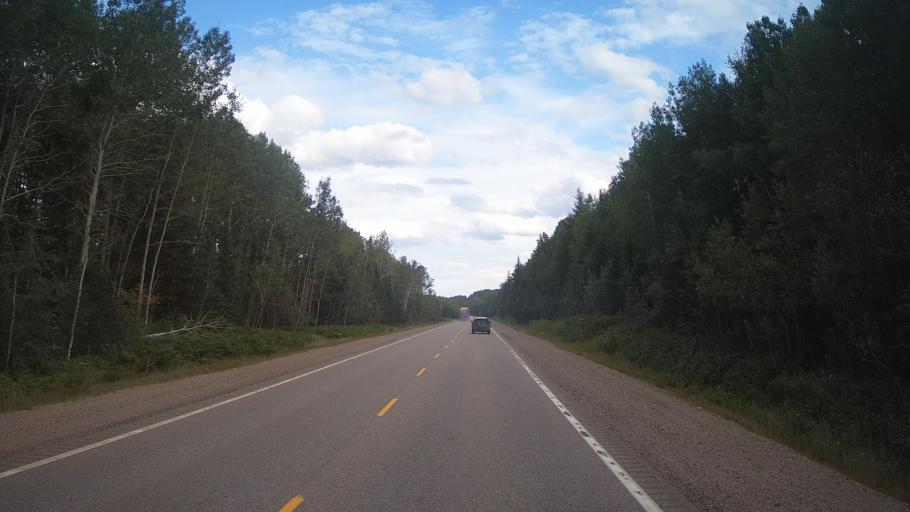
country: CA
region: Ontario
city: Mattawa
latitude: 46.2645
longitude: -78.3508
